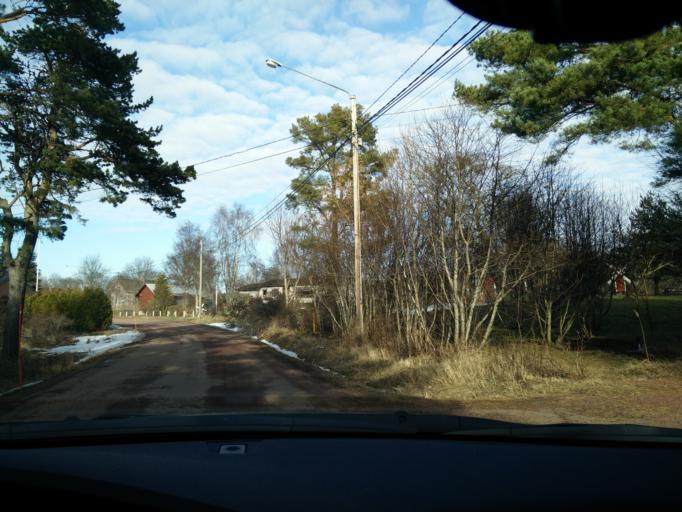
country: AX
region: Alands landsbygd
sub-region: Eckeroe
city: Eckeroe
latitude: 60.2217
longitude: 19.5526
